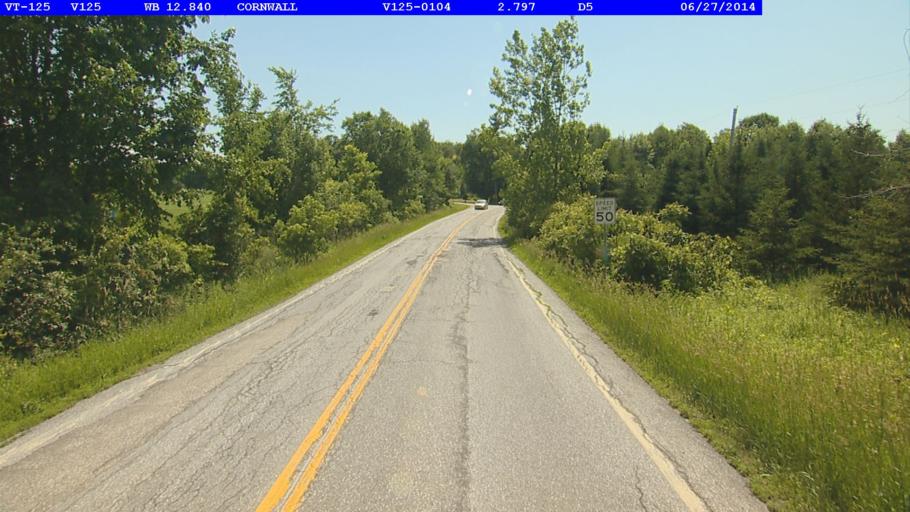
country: US
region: Vermont
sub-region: Addison County
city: Middlebury (village)
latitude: 44.0043
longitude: -73.2157
